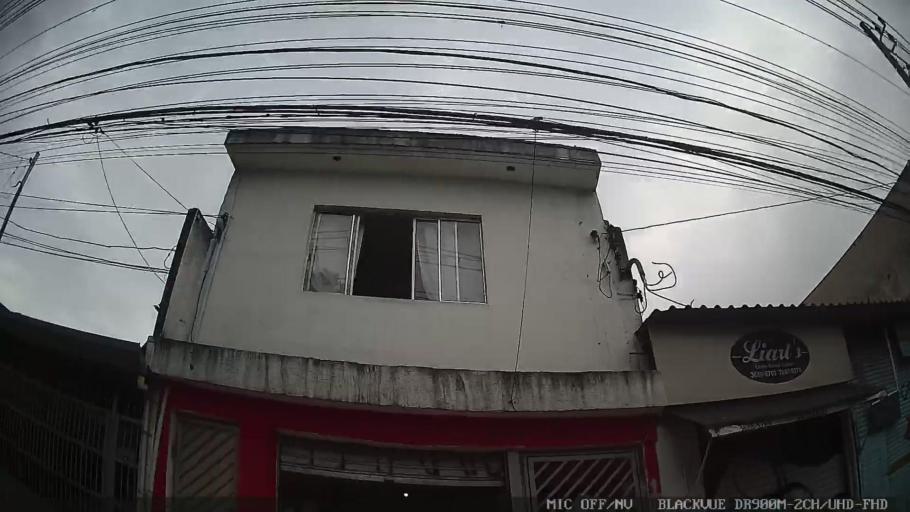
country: BR
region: Sao Paulo
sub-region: Osasco
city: Osasco
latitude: -23.4947
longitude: -46.7969
